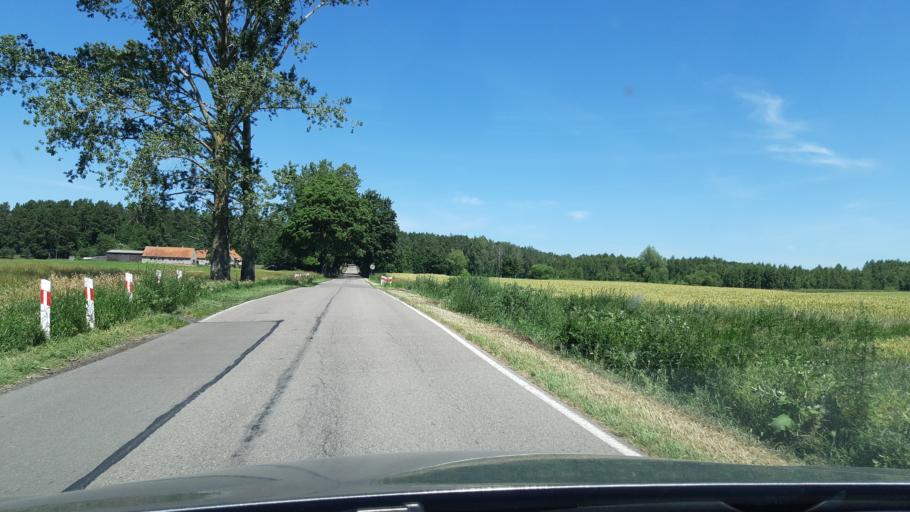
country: PL
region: Warmian-Masurian Voivodeship
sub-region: Powiat mragowski
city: Mikolajki
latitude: 53.8769
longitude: 21.6537
